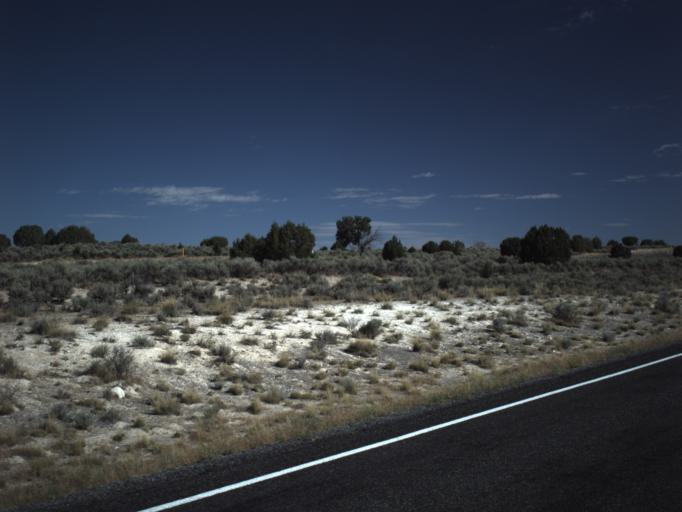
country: US
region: Utah
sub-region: Juab County
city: Mona
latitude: 39.7296
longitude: -112.1943
